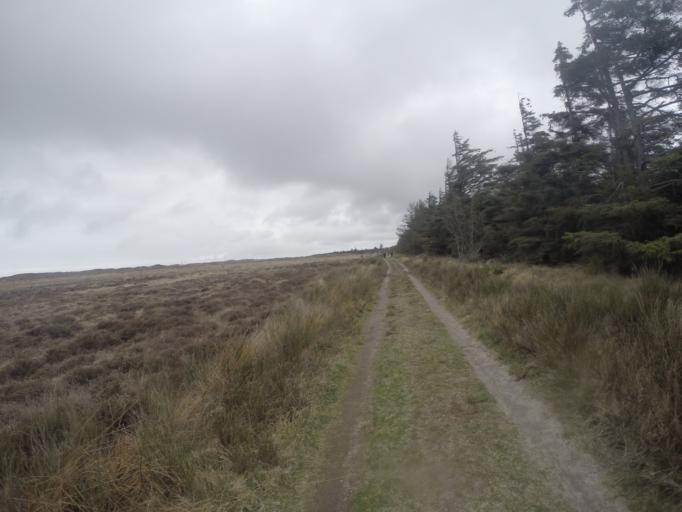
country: DK
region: North Denmark
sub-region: Thisted Kommune
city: Hurup
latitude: 56.9056
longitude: 8.3447
